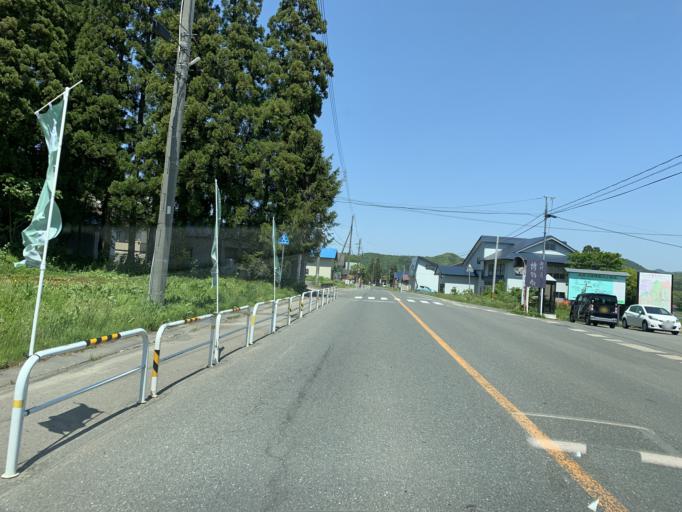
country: JP
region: Akita
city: Yokotemachi
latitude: 39.4264
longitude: 140.7483
